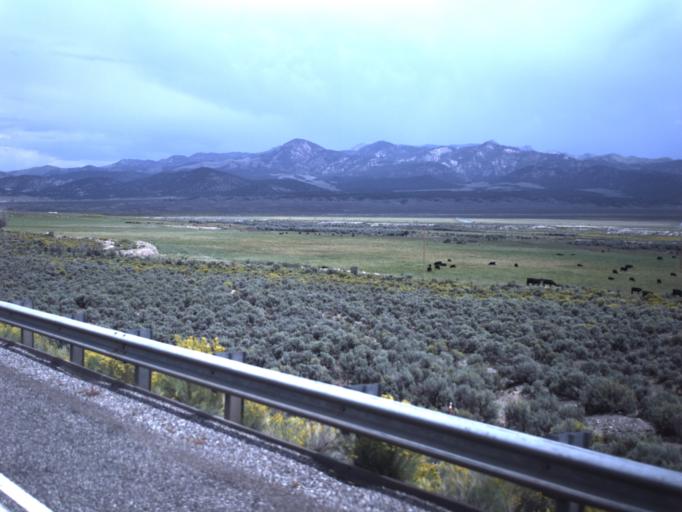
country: US
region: Utah
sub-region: Garfield County
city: Panguitch
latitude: 37.9711
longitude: -112.4088
